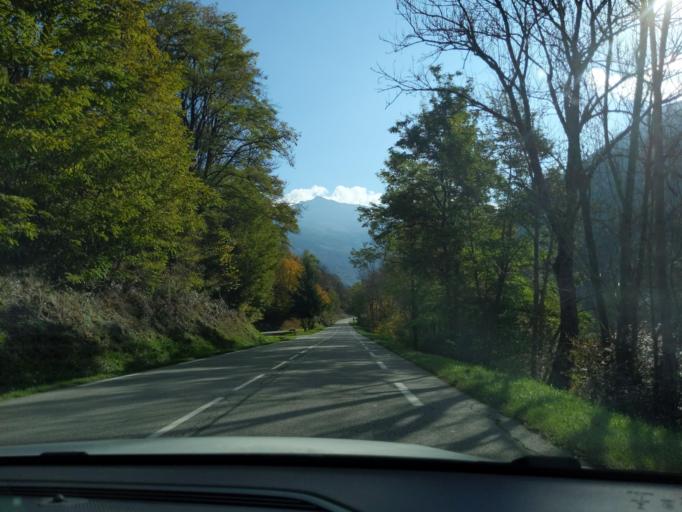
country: FR
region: Rhone-Alpes
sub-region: Departement de la Savoie
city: Seez
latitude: 45.6168
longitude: 6.8173
